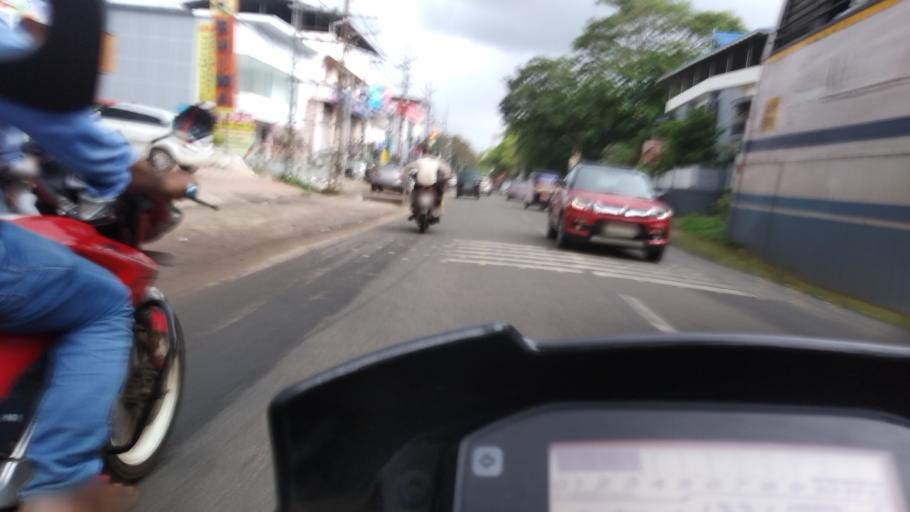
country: IN
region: Kerala
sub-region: Thiruvananthapuram
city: Attingal
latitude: 8.7042
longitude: 76.8148
